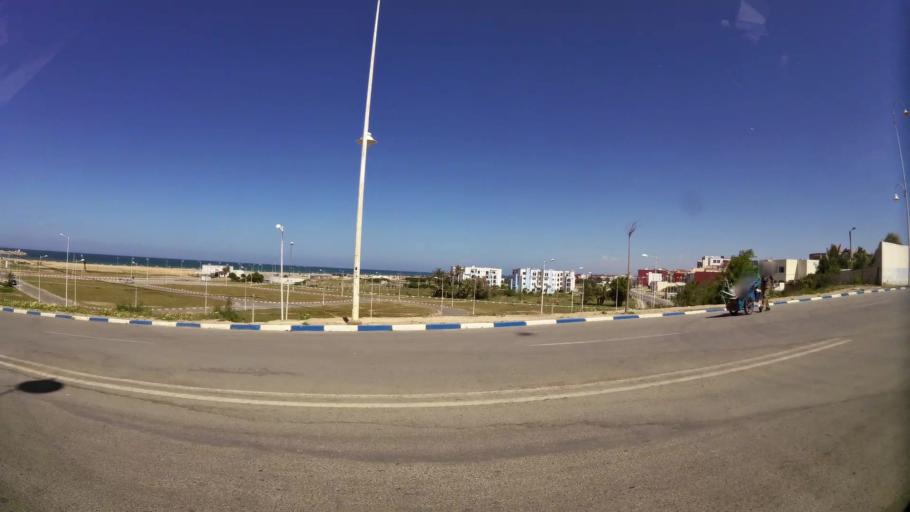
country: MA
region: Oriental
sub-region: Berkane-Taourirt
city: Madagh
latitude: 35.1394
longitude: -2.4239
